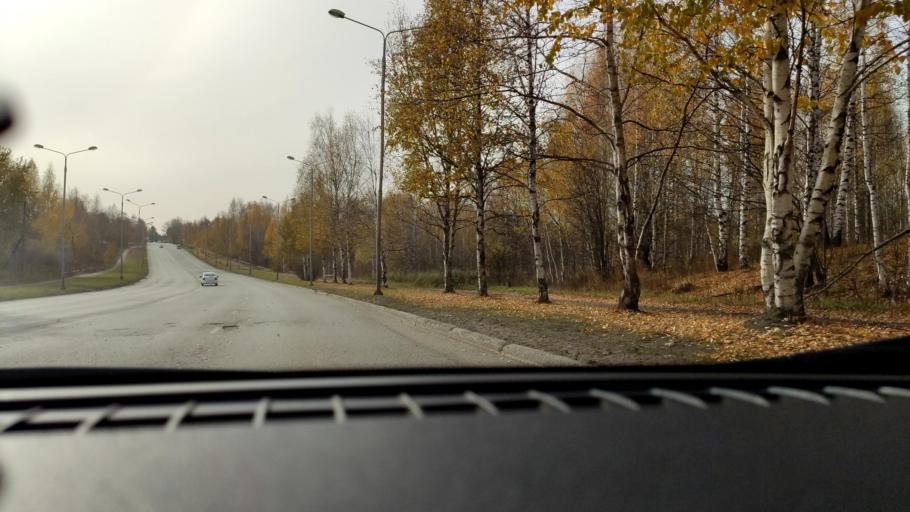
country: RU
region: Perm
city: Perm
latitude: 58.0981
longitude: 56.3859
